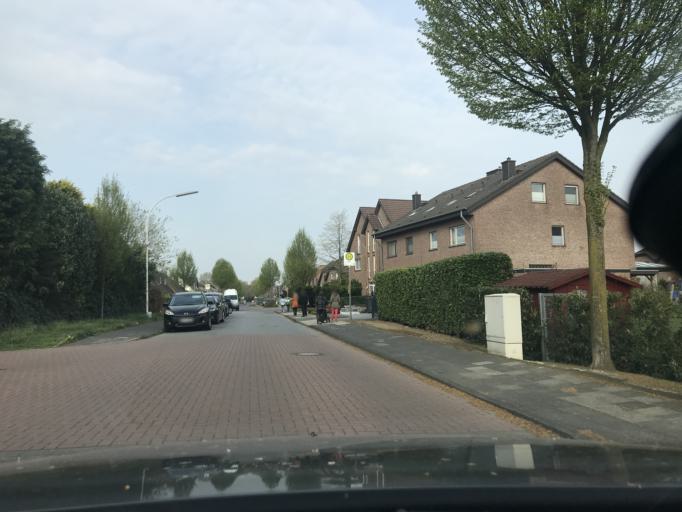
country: DE
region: North Rhine-Westphalia
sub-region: Regierungsbezirk Dusseldorf
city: Wachtendonk
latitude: 51.4116
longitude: 6.3427
